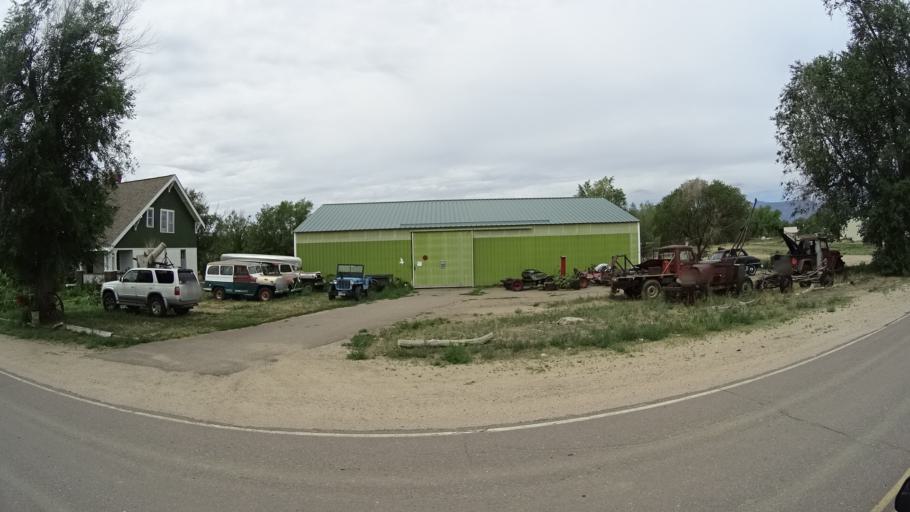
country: US
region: Colorado
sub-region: El Paso County
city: Fountain
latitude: 38.6693
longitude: -104.6946
